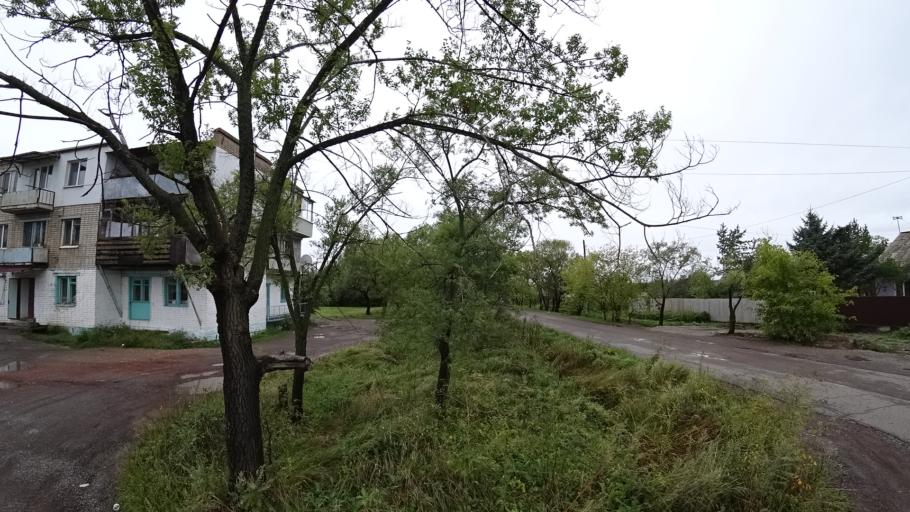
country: RU
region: Primorskiy
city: Monastyrishche
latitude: 44.2010
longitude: 132.4961
